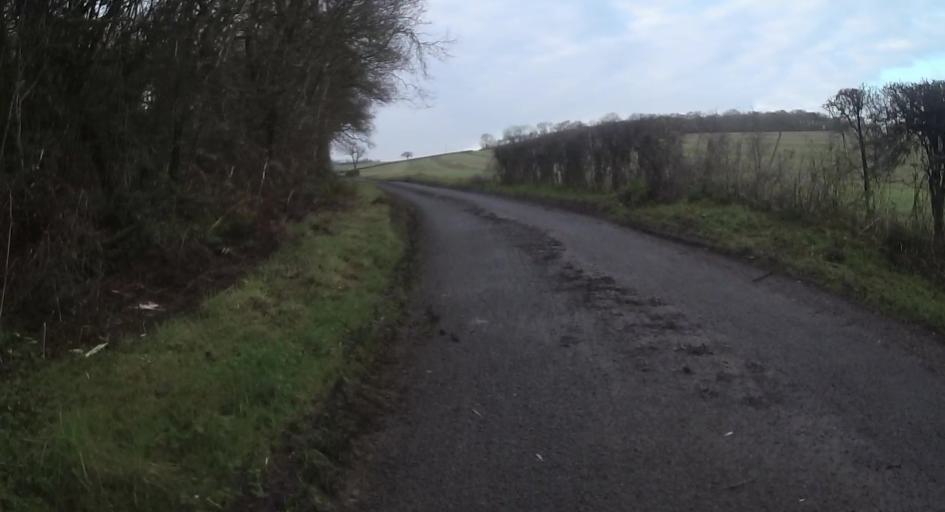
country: GB
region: England
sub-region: Hampshire
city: Kingsclere
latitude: 51.2913
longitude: -1.1994
